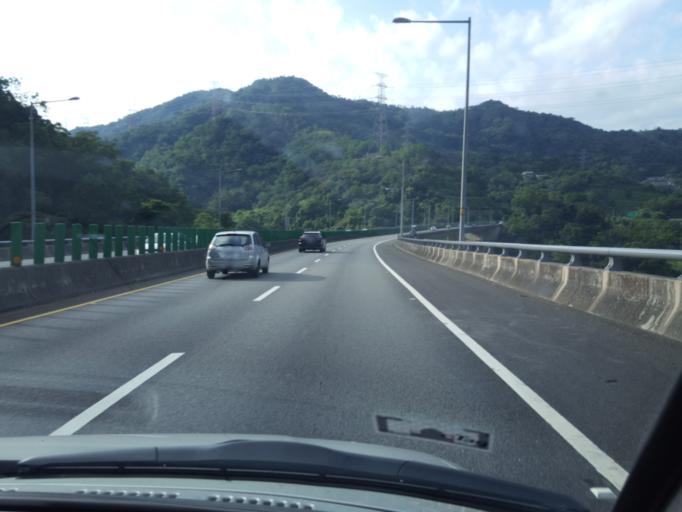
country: TW
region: Taipei
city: Taipei
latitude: 24.9904
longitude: 121.6566
